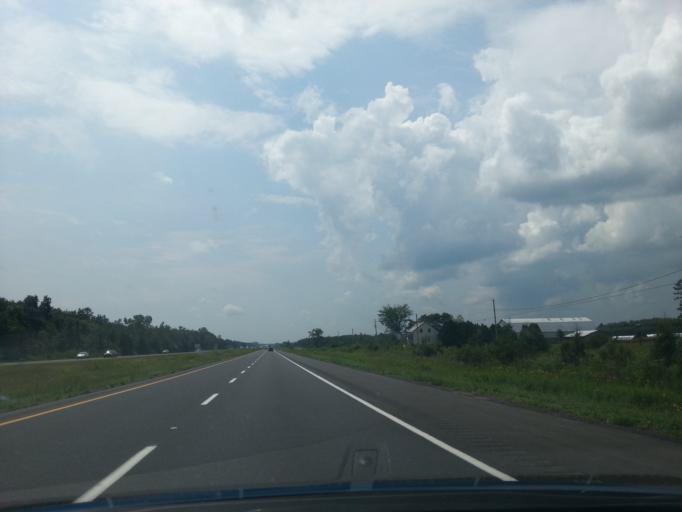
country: CA
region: Quebec
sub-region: Chaudiere-Appalaches
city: Saint-Antoine-de-Tilly
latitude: 46.5163
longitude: -71.6543
